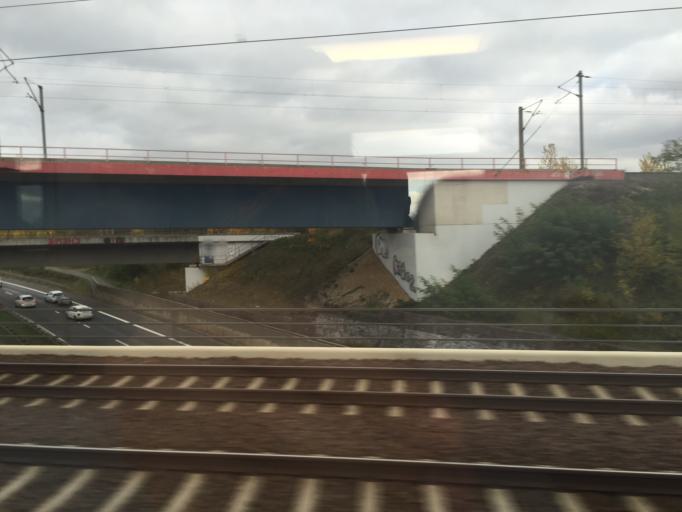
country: DE
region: Saxony
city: Rackwitz
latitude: 51.3892
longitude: 12.3919
